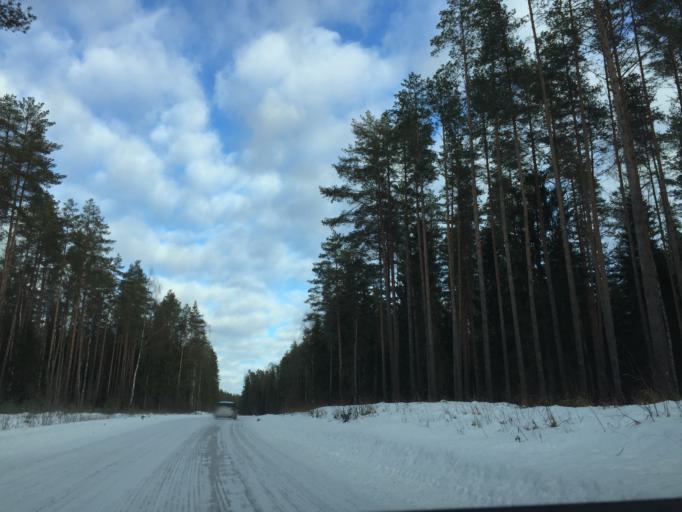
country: LV
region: Ogre
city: Jumprava
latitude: 56.5527
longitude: 24.8977
